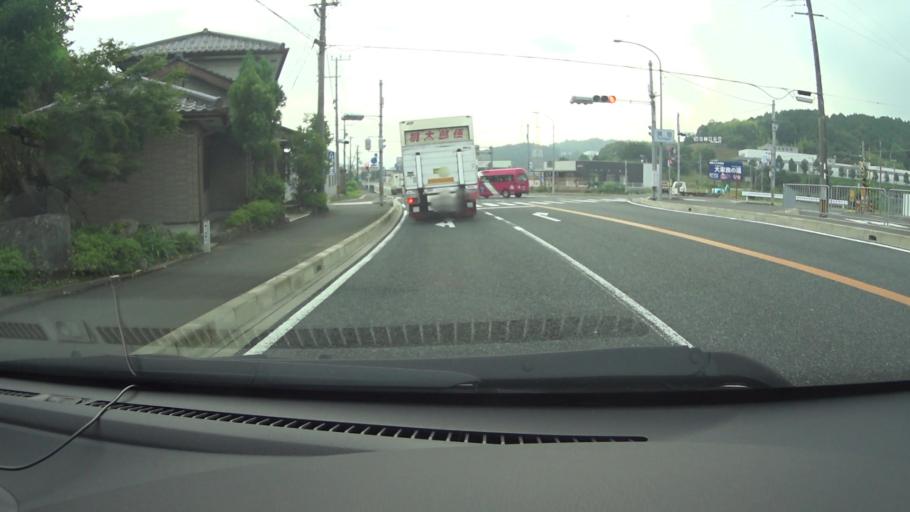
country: JP
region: Kyoto
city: Ayabe
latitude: 35.3278
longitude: 135.2940
